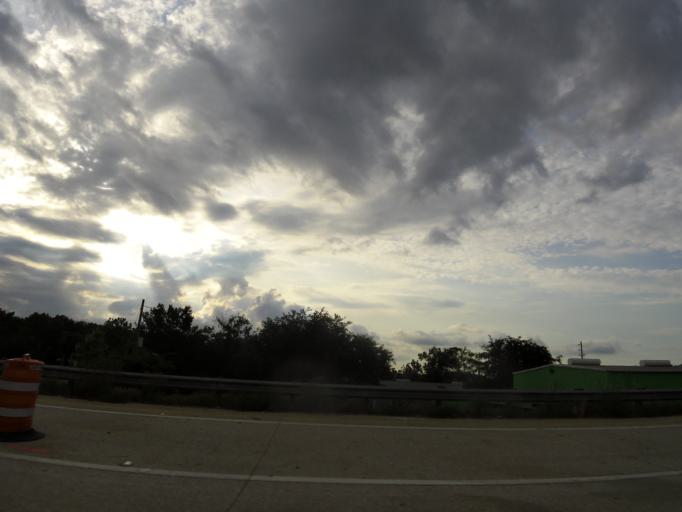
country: US
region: Florida
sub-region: Duval County
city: Jacksonville
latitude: 30.3272
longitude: -81.6792
